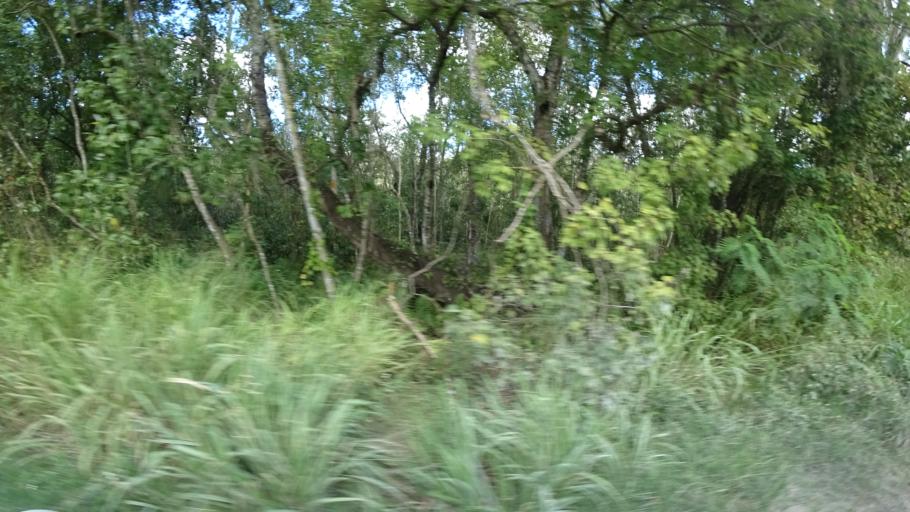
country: US
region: Florida
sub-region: Sarasota County
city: Lake Sarasota
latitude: 27.3204
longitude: -82.2639
